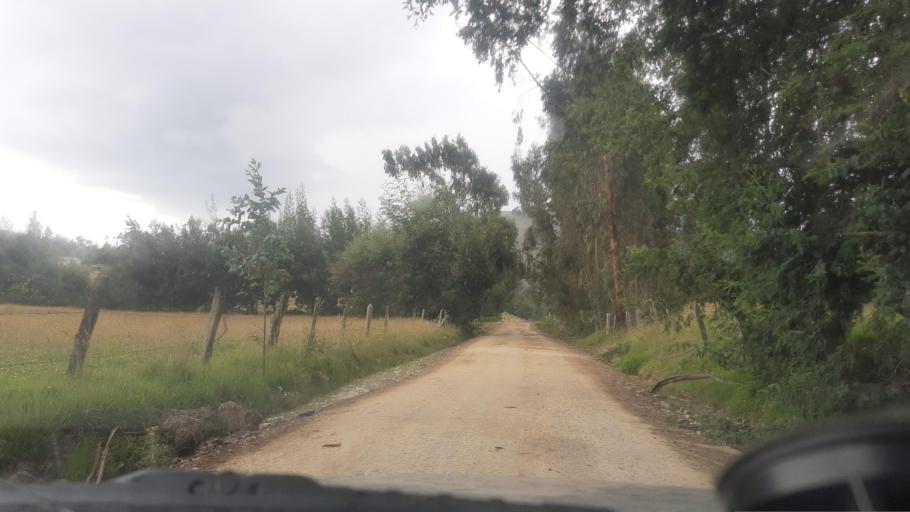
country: CO
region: Cundinamarca
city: Cucunuba
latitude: 5.1921
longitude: -73.7932
